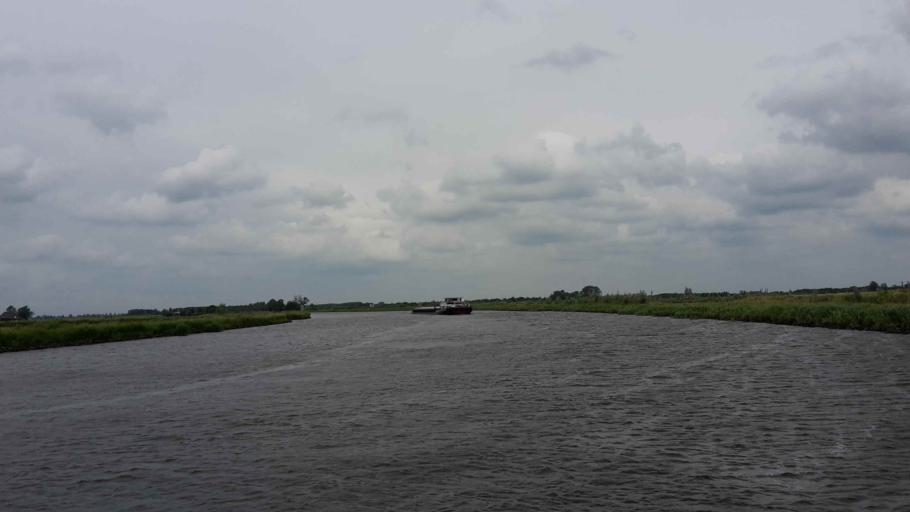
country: NL
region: Friesland
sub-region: Gemeente Boarnsterhim
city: Grou
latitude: 53.1141
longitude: 5.8746
